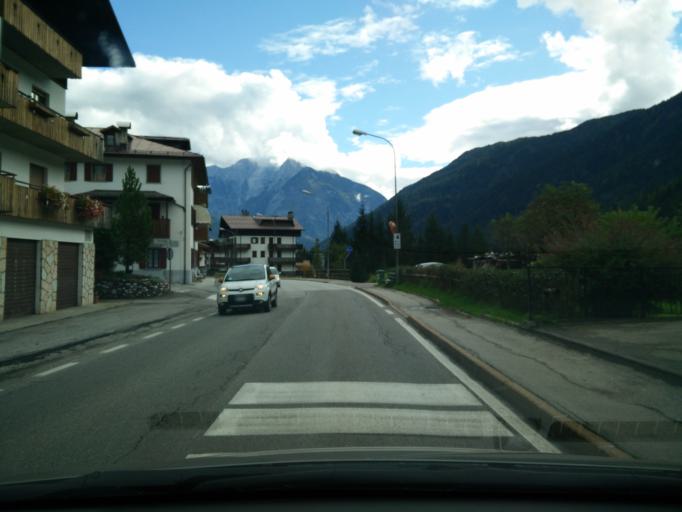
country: IT
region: Veneto
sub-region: Provincia di Belluno
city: Auronzo
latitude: 46.5585
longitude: 12.4234
